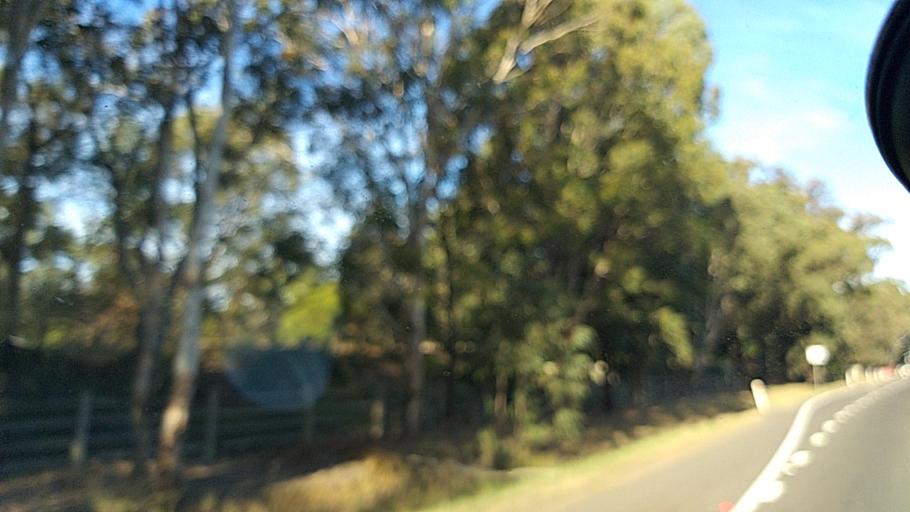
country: AU
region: New South Wales
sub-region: Hawkesbury
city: South Windsor
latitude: -33.6620
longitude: 150.7981
